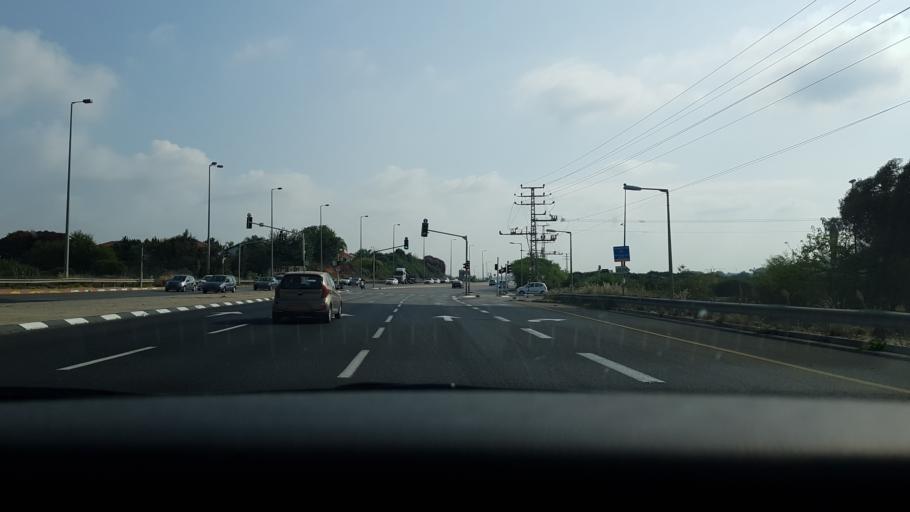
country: IL
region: Central District
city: Ness Ziona
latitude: 31.9209
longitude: 34.7777
